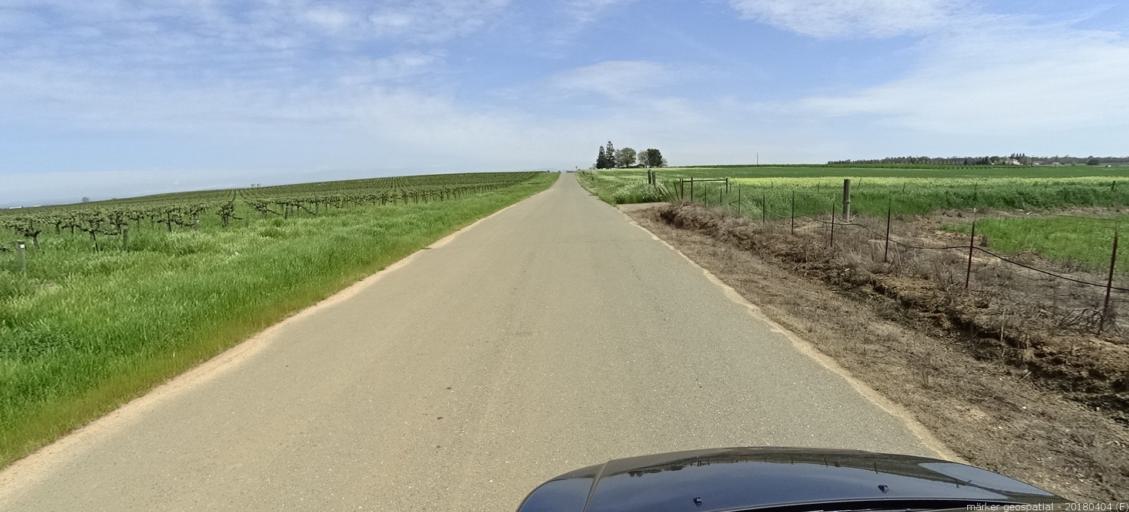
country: US
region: California
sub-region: Sacramento County
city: Herald
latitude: 38.3069
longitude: -121.2037
